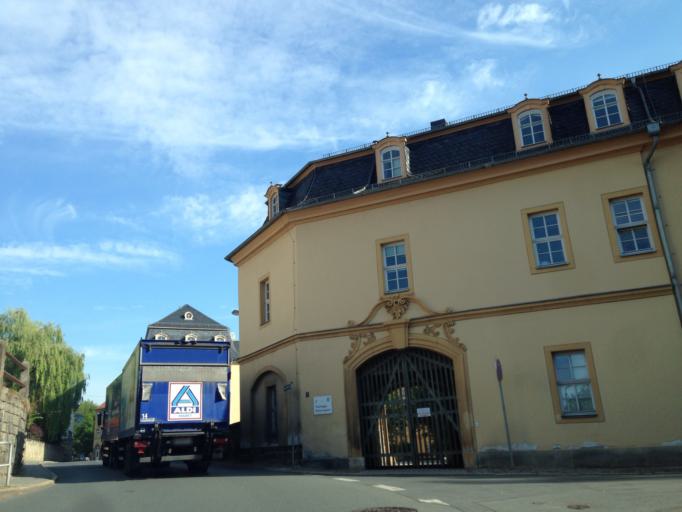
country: DE
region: Thuringia
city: Rudolstadt
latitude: 50.7219
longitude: 11.3435
